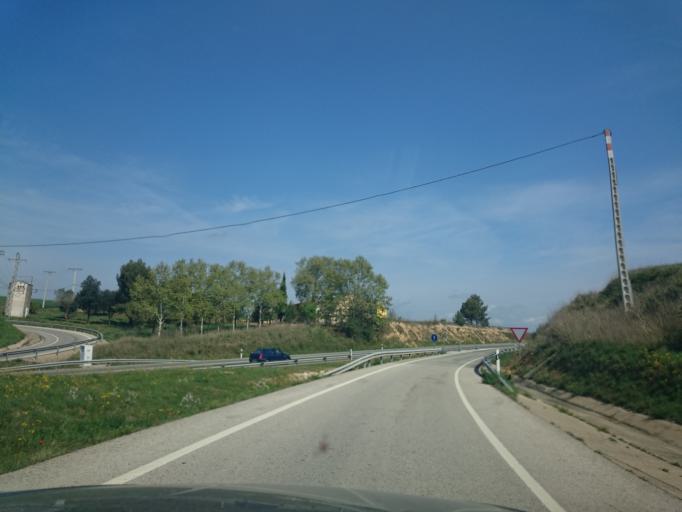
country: ES
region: Catalonia
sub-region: Provincia de Girona
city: Vilademuls
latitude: 42.1315
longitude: 2.9036
